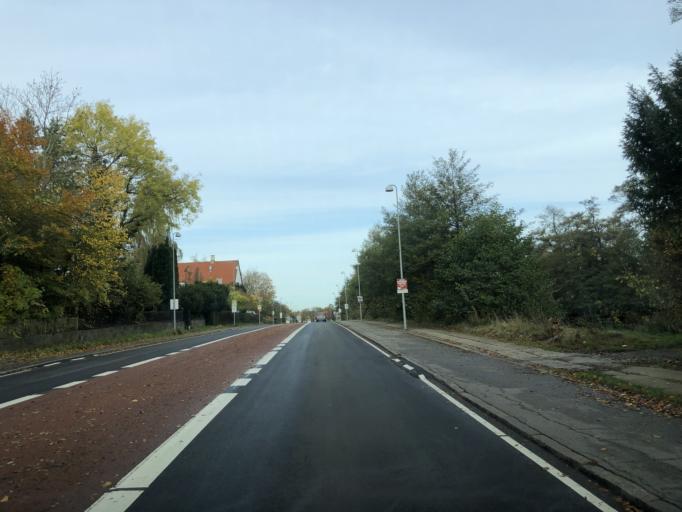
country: DK
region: Capital Region
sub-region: Hillerod Kommune
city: Hillerod
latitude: 55.9298
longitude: 12.3185
